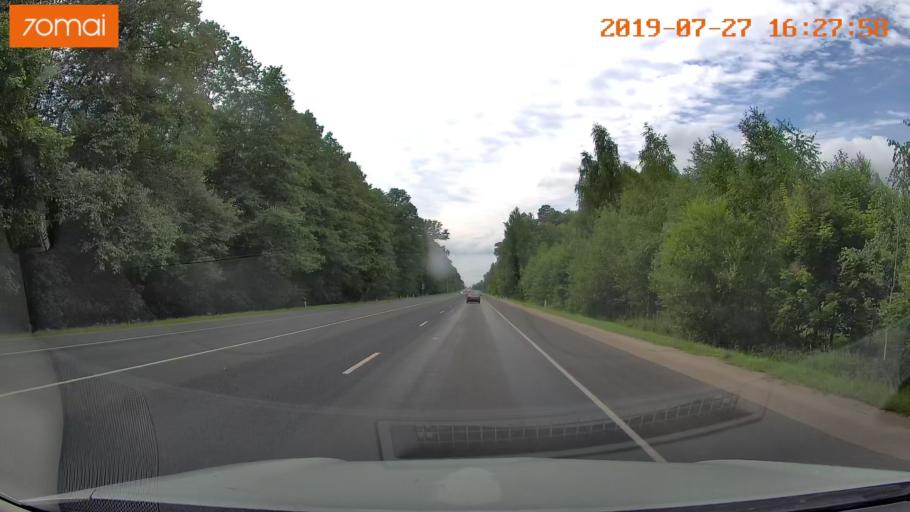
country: RU
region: Kaliningrad
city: Zheleznodorozhnyy
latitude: 54.6464
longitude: 21.3708
